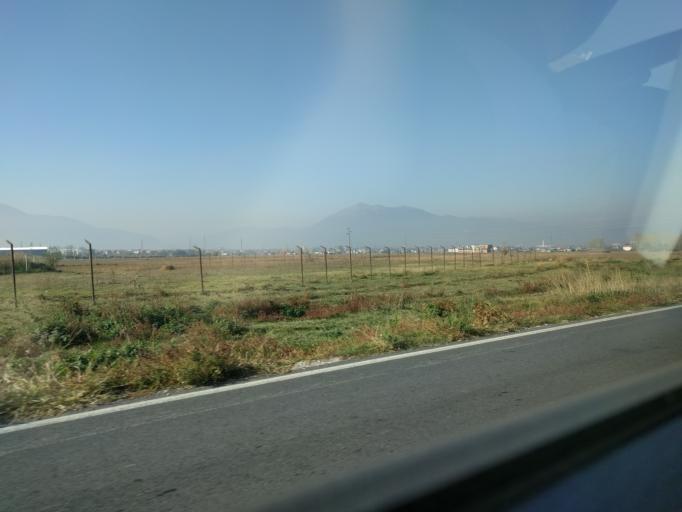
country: XK
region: Prizren
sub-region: Prizren
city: Prizren
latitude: 42.2387
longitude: 20.7565
